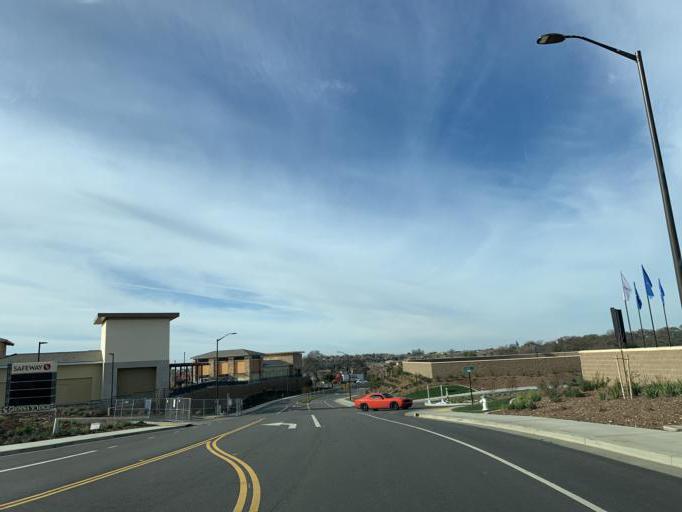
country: US
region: California
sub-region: El Dorado County
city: Cameron Park
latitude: 38.6758
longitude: -121.0268
